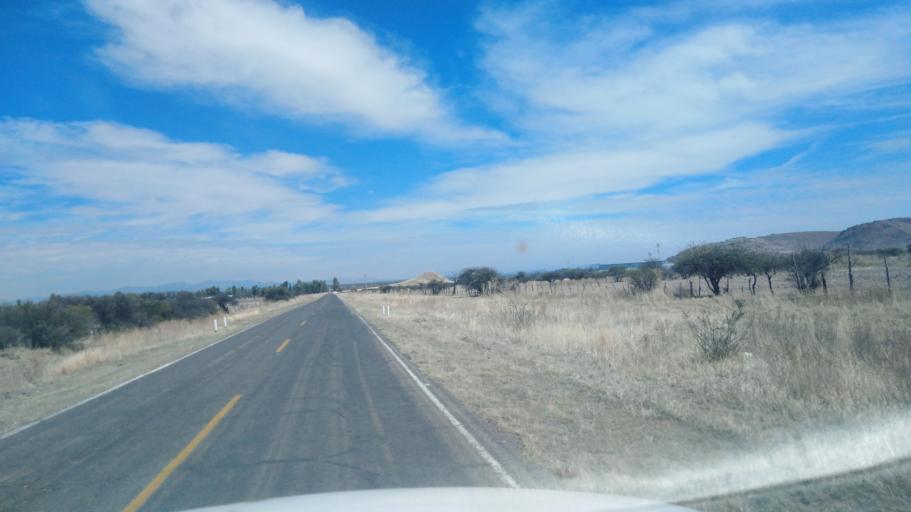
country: MX
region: Durango
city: Victoria de Durango
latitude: 24.1787
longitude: -104.6898
